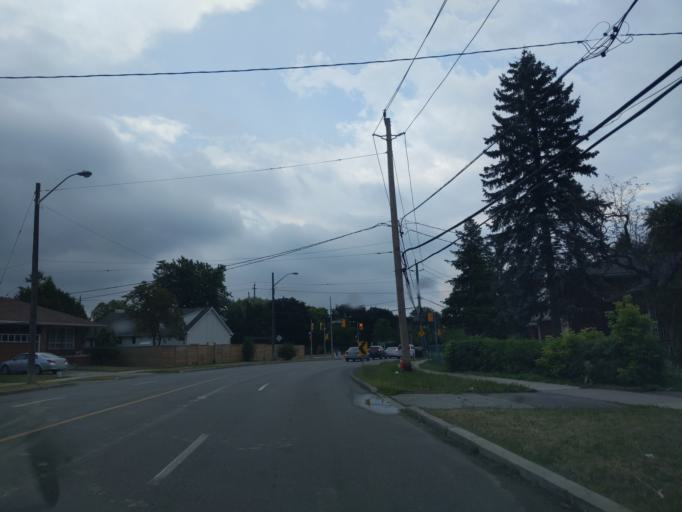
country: CA
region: Ontario
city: North York
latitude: 43.7894
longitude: -79.4105
